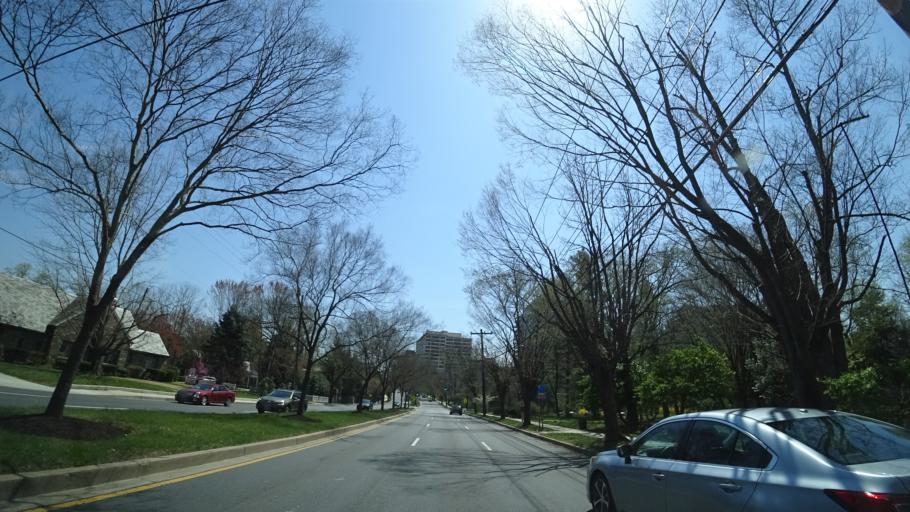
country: US
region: Maryland
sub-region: Montgomery County
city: Friendship Village
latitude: 38.9683
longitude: -77.0890
